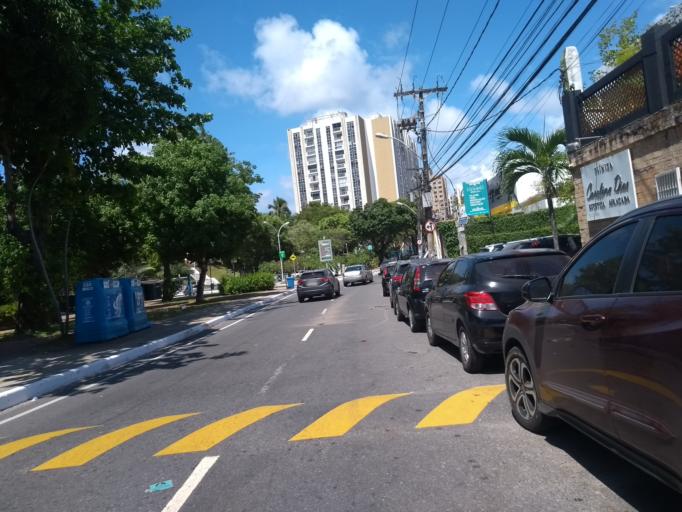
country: BR
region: Bahia
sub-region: Salvador
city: Salvador
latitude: -12.9942
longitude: -38.4592
